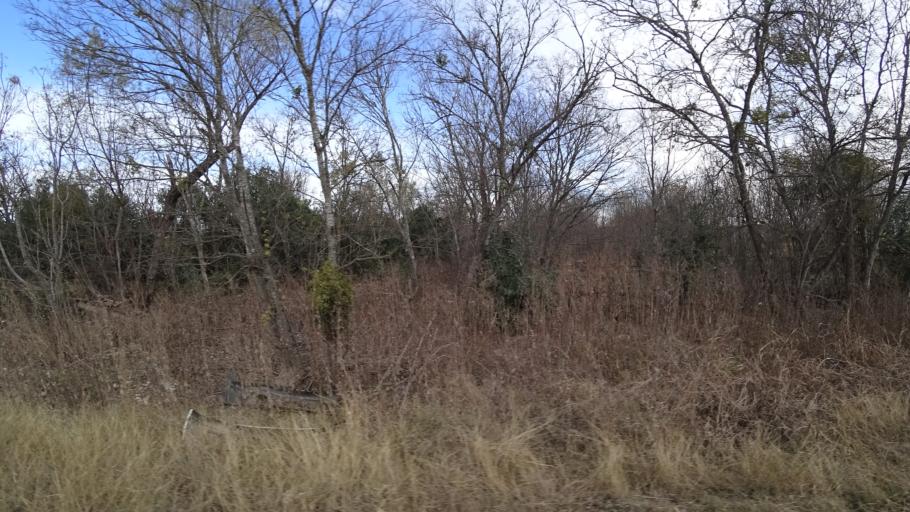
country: US
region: Texas
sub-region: Travis County
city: Onion Creek
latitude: 30.1555
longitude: -97.7215
